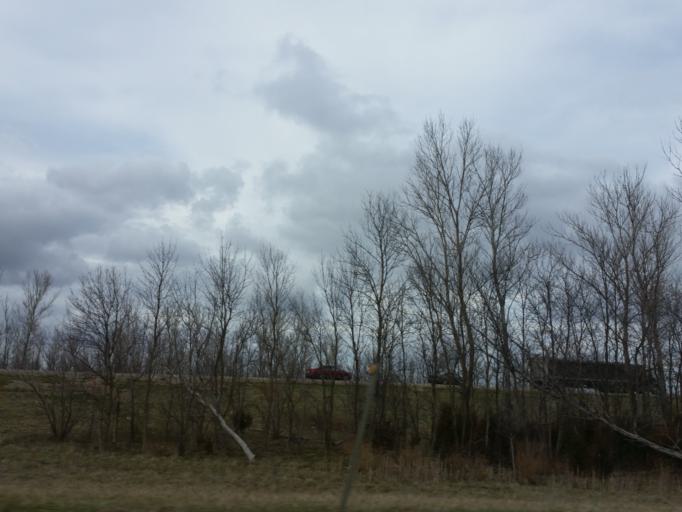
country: US
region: Iowa
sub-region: Black Hawk County
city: Elk Run Heights
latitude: 42.4488
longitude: -92.1963
